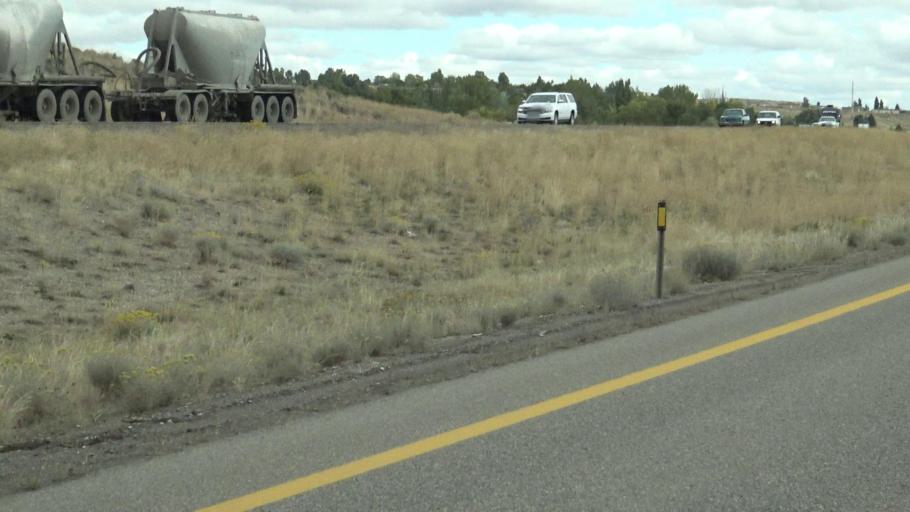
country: US
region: Nevada
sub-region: Elko County
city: Elko
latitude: 40.8379
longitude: -115.7799
